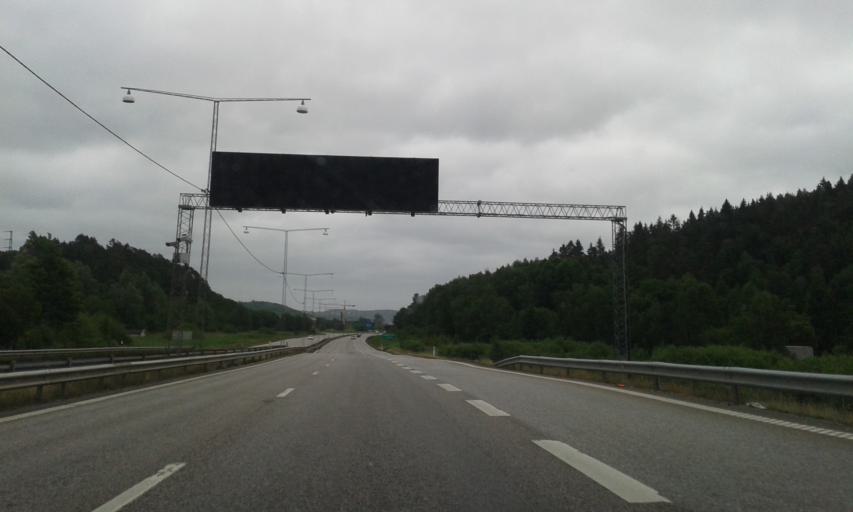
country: SE
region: Vaestra Goetaland
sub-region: Kungalvs Kommun
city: Kungalv
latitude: 57.8804
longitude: 11.9528
